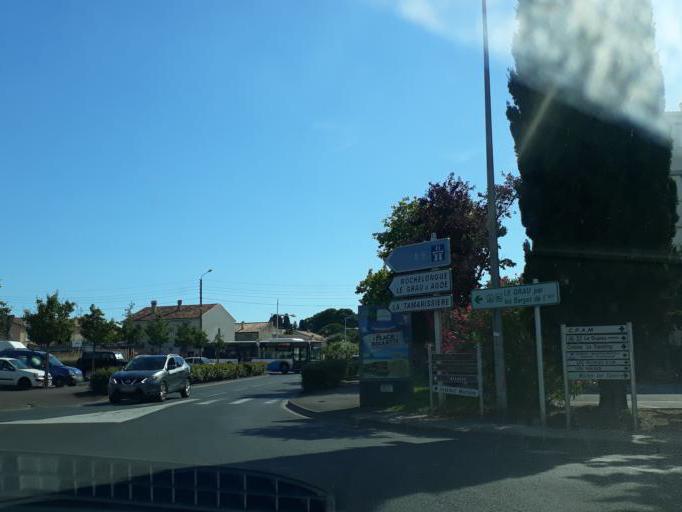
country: FR
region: Languedoc-Roussillon
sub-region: Departement de l'Herault
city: Agde
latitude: 43.3089
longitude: 3.4768
